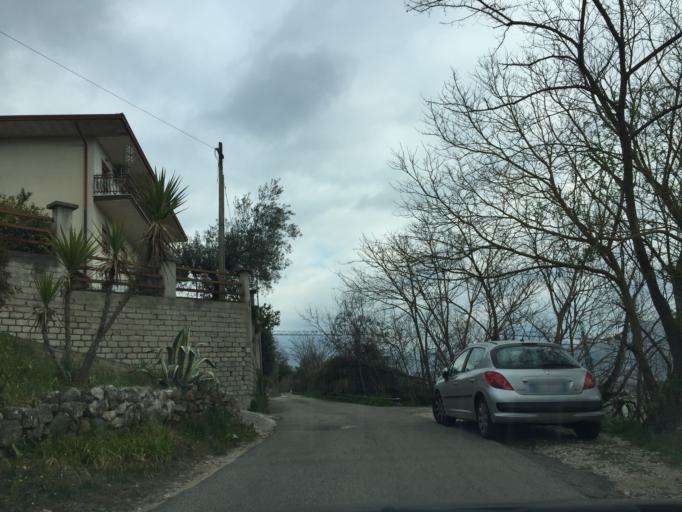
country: IT
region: Latium
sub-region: Provincia di Frosinone
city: Cassino
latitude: 41.4812
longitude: 13.8145
